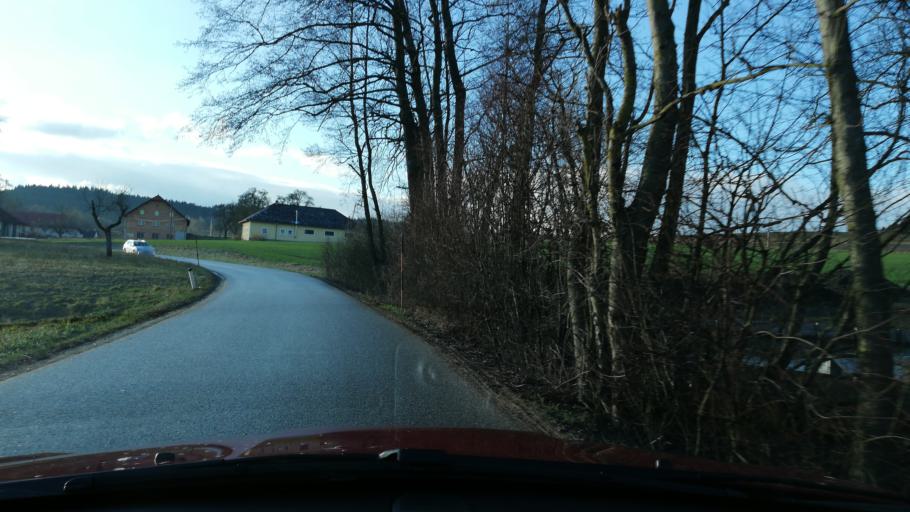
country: AT
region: Upper Austria
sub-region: Wels-Land
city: Buchkirchen
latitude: 48.1994
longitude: 13.9770
